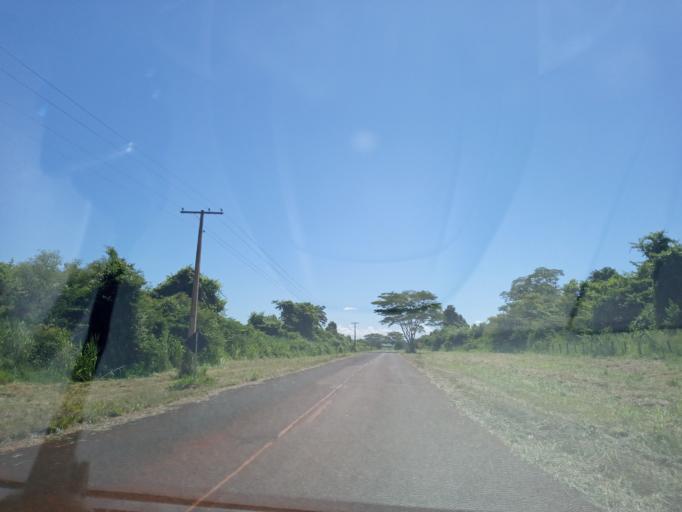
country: BR
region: Goias
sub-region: Itumbiara
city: Itumbiara
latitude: -18.4158
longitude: -49.1328
